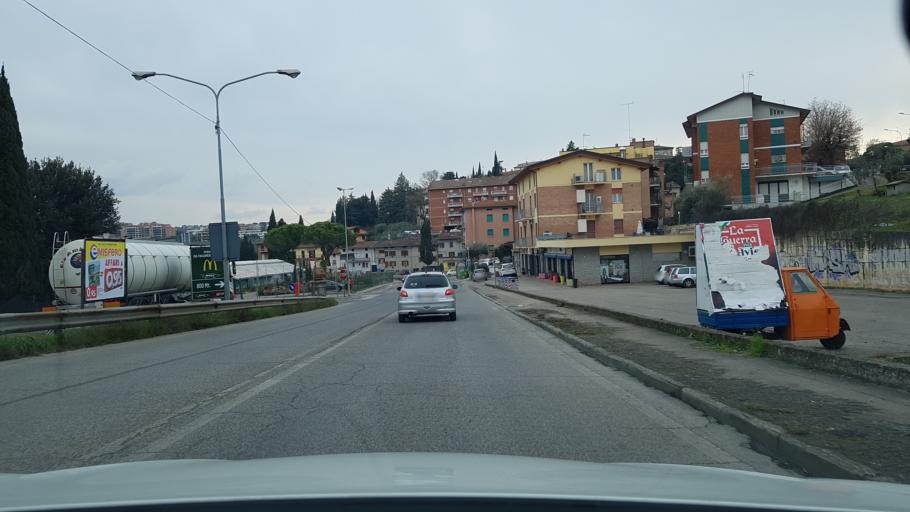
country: IT
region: Umbria
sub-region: Provincia di Perugia
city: Lacugnano
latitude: 43.1061
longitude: 12.3529
